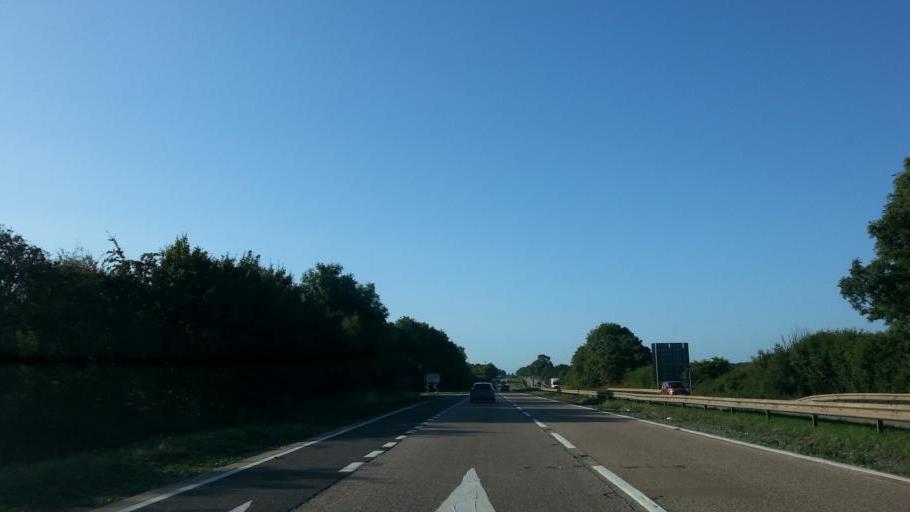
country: GB
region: England
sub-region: Leicestershire
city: Grimston
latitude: 52.7967
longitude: -1.0434
